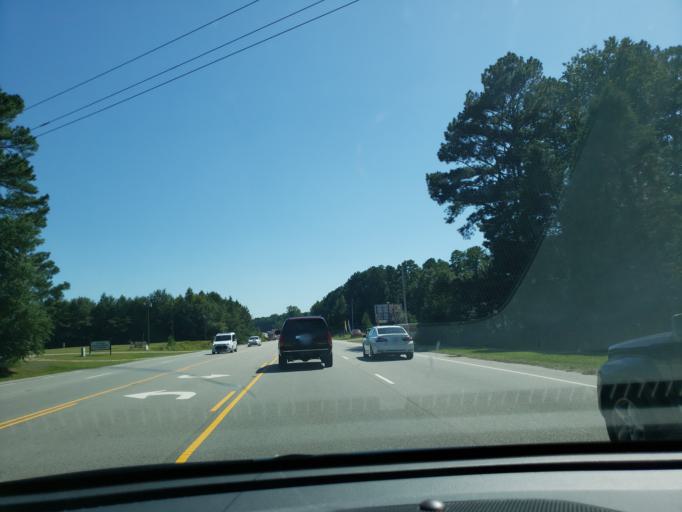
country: US
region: North Carolina
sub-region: Lee County
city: Broadway
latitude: 35.3788
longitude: -79.1099
